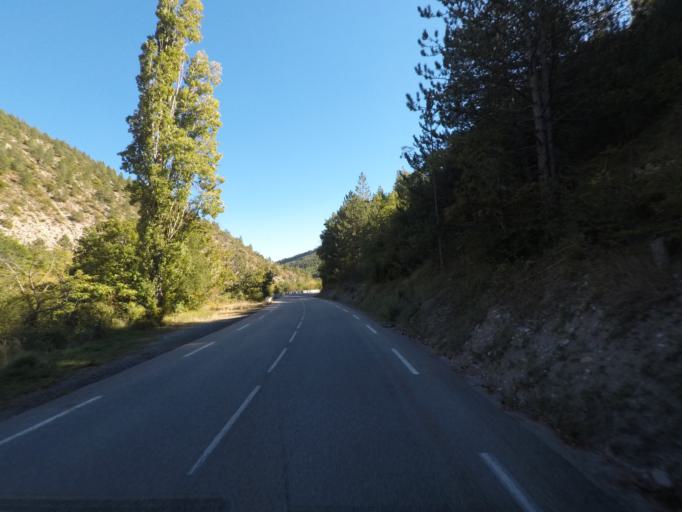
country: FR
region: Rhone-Alpes
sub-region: Departement de la Drome
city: Buis-les-Baronnies
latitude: 44.3839
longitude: 5.3960
